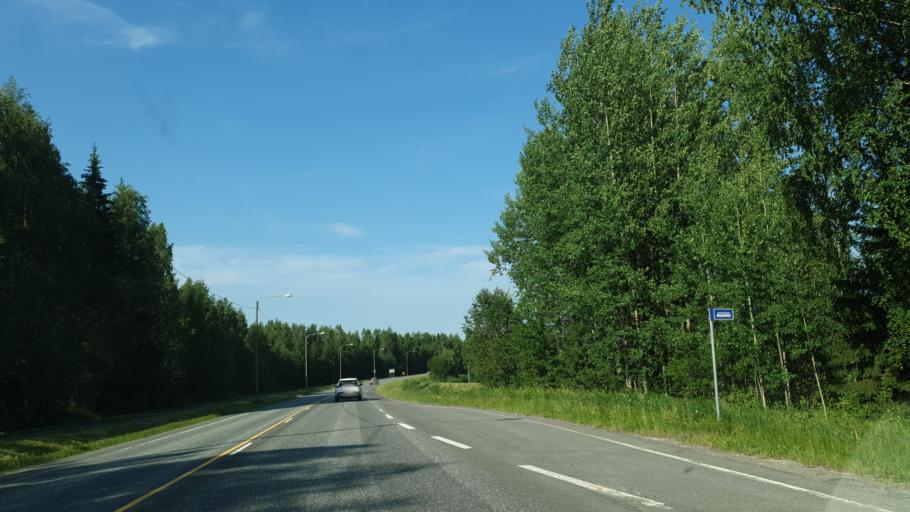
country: FI
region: Northern Savo
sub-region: Kuopio
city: Siilinjaervi
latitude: 63.1282
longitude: 27.7736
